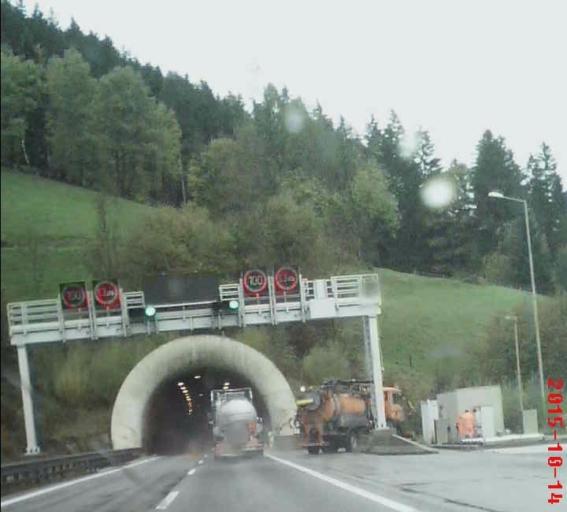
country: AT
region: Styria
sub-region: Politischer Bezirk Liezen
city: Selzthal
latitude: 47.5378
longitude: 14.3075
